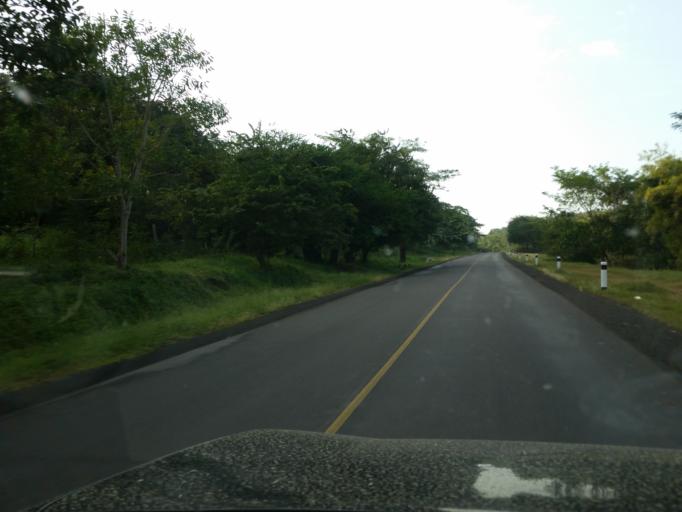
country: NI
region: Rio San Juan
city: San Miguelito
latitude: 11.3784
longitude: -84.7845
